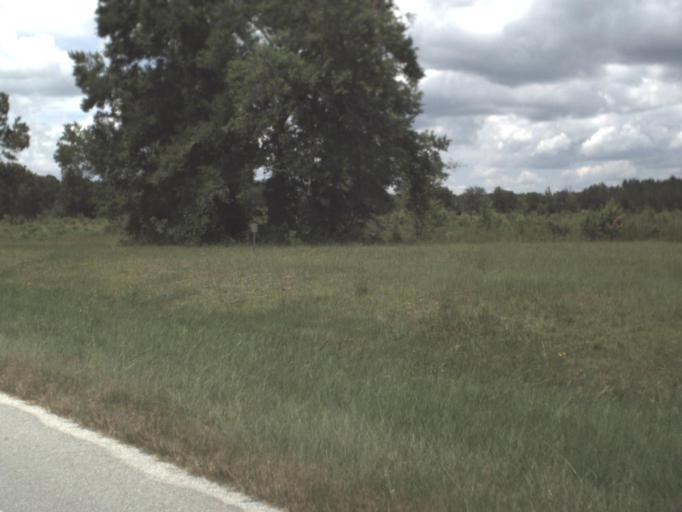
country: US
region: Florida
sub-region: Alachua County
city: Newberry
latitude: 29.6729
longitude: -82.6070
